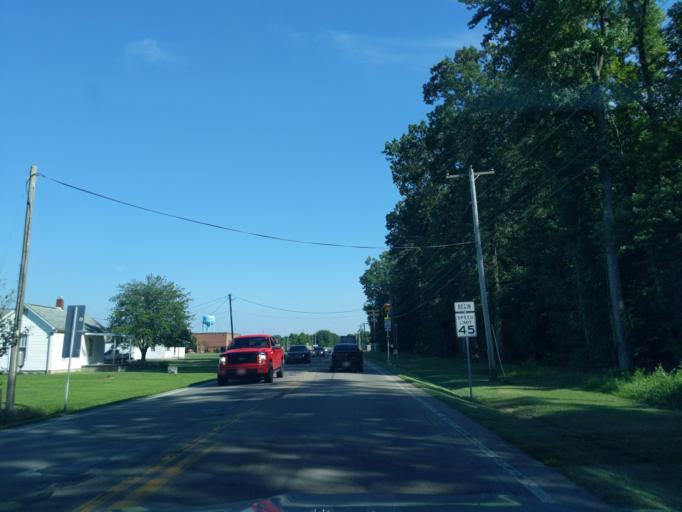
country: US
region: Indiana
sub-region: Ripley County
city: Osgood
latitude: 39.1436
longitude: -85.2975
